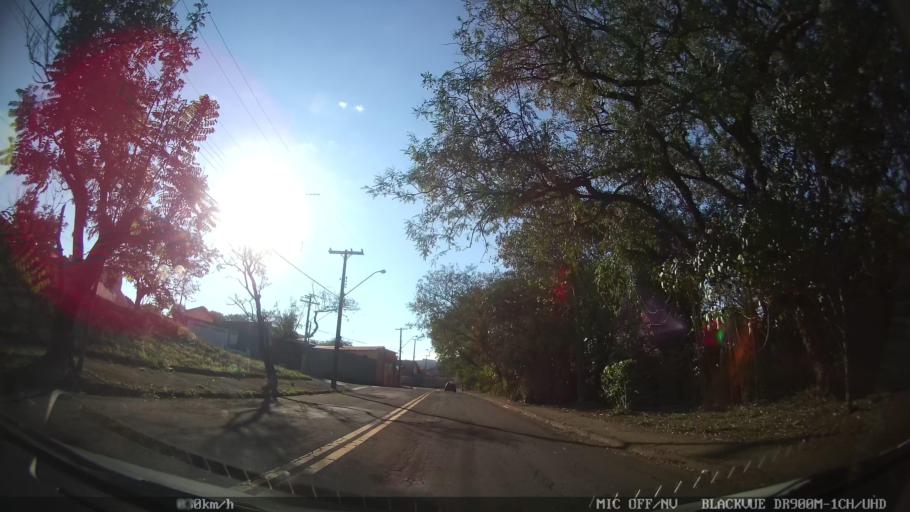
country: BR
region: Sao Paulo
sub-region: Piracicaba
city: Piracicaba
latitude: -22.6823
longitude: -47.6336
